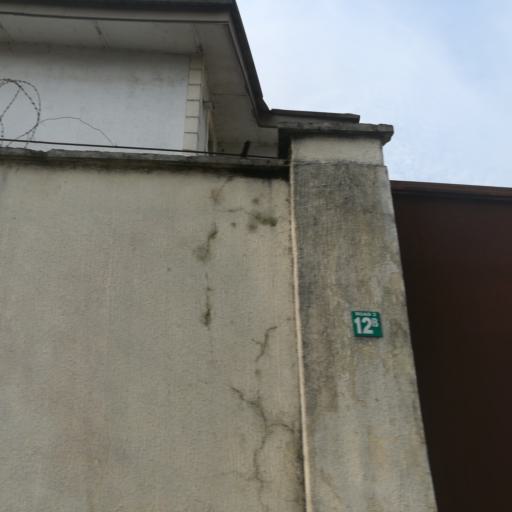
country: NG
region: Rivers
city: Port Harcourt
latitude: 4.8474
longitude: 7.0556
